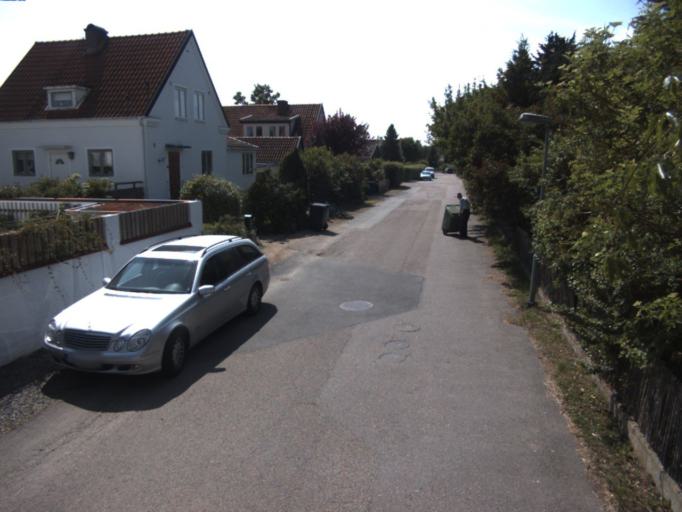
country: SE
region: Skane
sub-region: Helsingborg
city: Helsingborg
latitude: 56.0888
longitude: 12.6582
